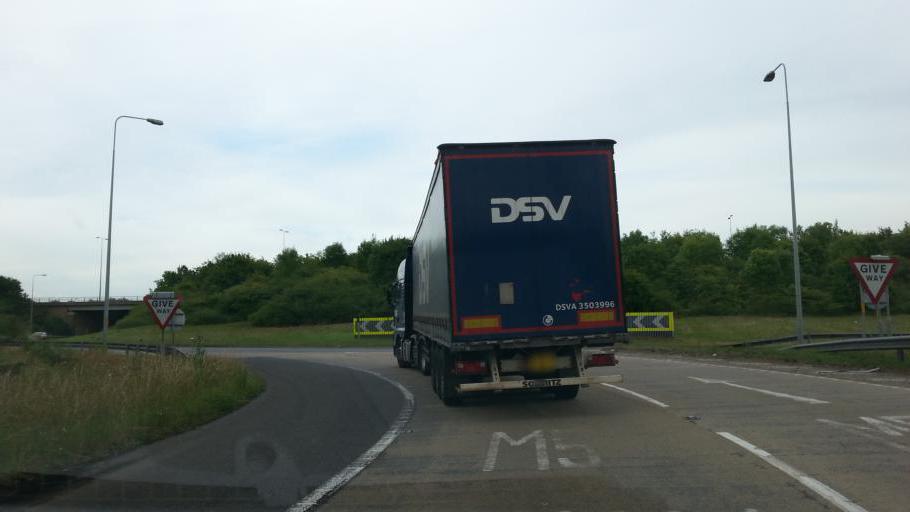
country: GB
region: England
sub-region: Worcestershire
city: Bredon
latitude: 52.0473
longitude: -2.1376
